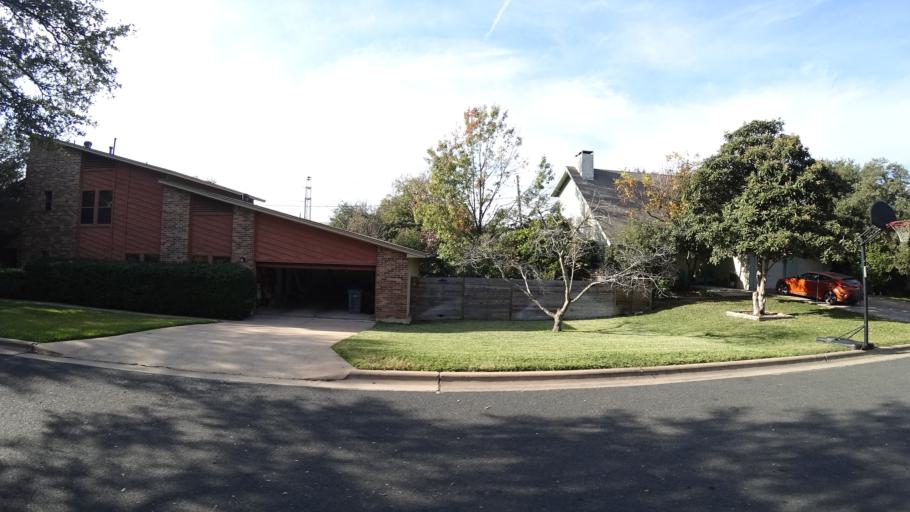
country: US
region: Texas
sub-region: Williamson County
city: Jollyville
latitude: 30.3861
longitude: -97.7483
